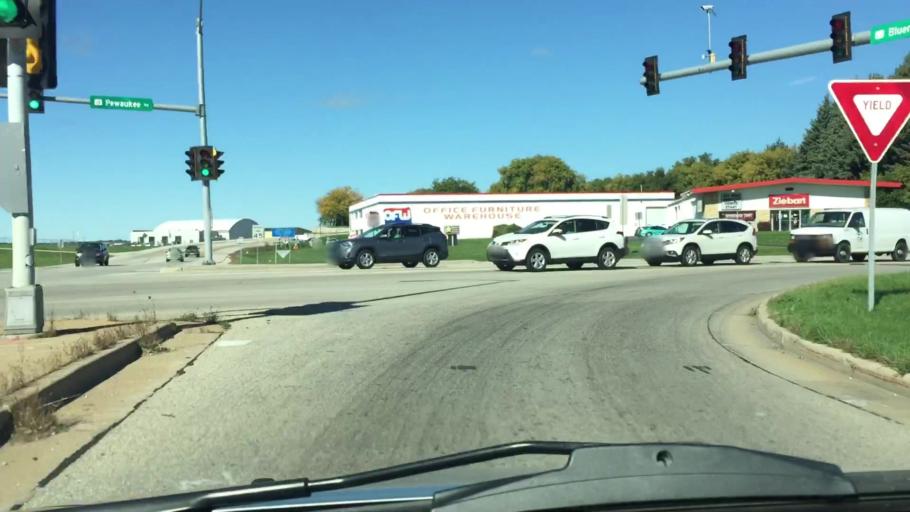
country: US
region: Wisconsin
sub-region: Waukesha County
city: Waukesha
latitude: 43.0421
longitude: -88.2253
